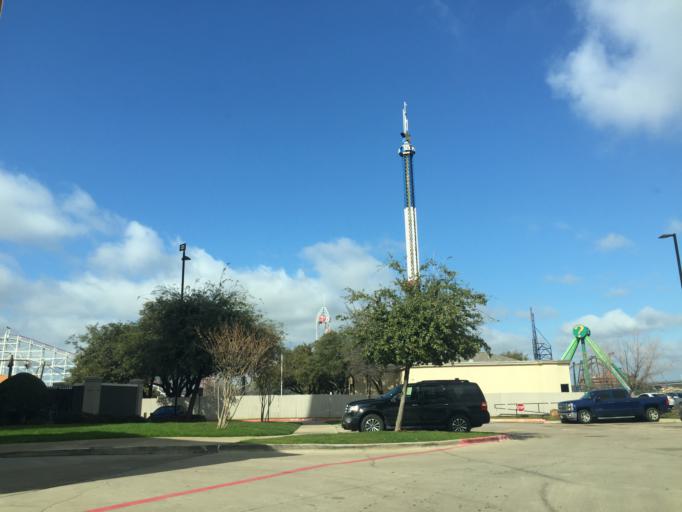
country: US
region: Texas
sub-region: Tarrant County
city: Arlington
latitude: 32.7551
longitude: -97.0656
